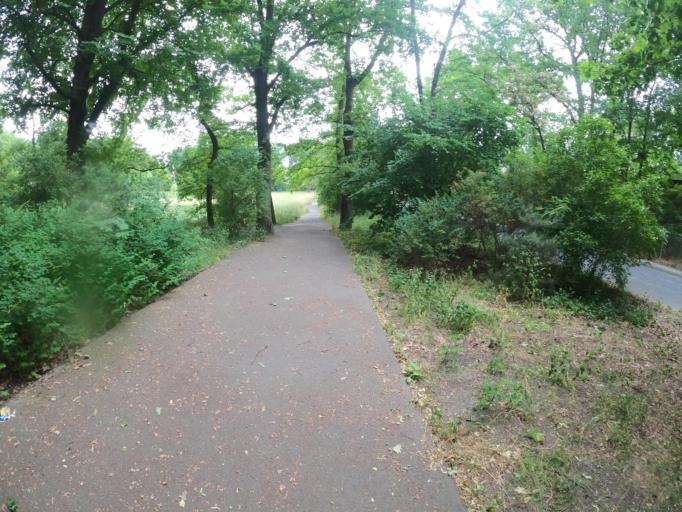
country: DE
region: Berlin
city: Haselhorst
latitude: 52.5249
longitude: 13.2430
